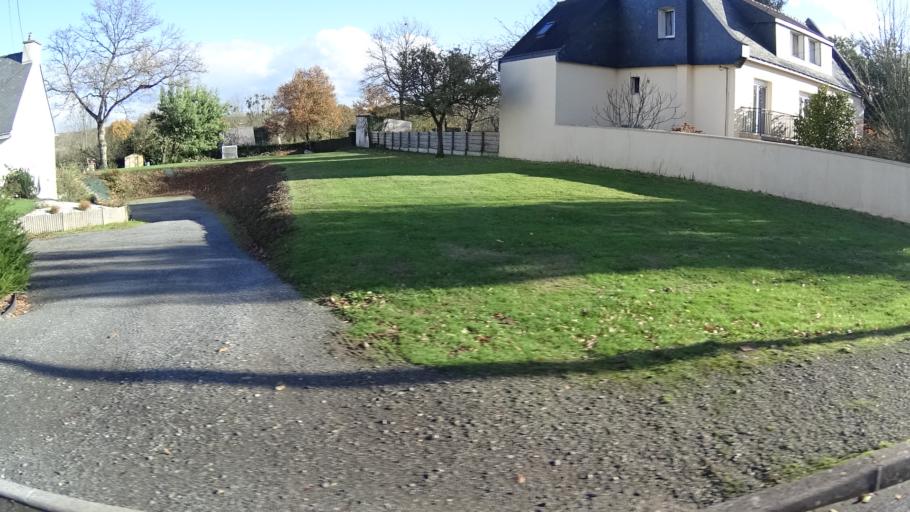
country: FR
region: Brittany
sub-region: Departement du Morbihan
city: Saint-Perreux
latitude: 47.6710
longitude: -2.1074
